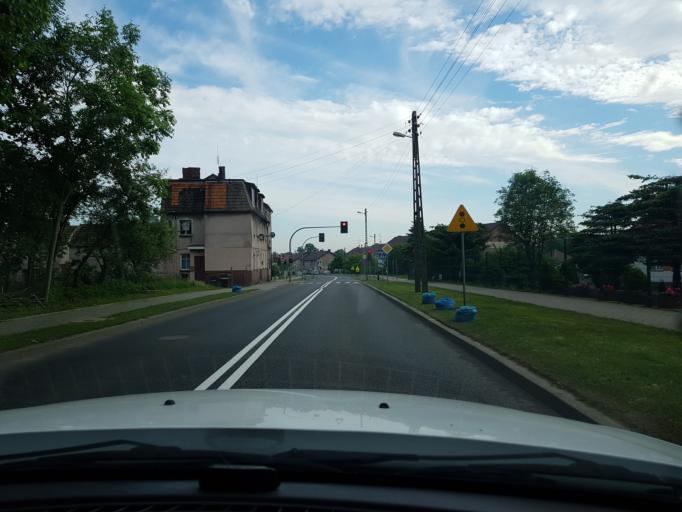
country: PL
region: West Pomeranian Voivodeship
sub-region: Powiat stargardzki
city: Chociwel
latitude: 53.4593
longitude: 15.3326
